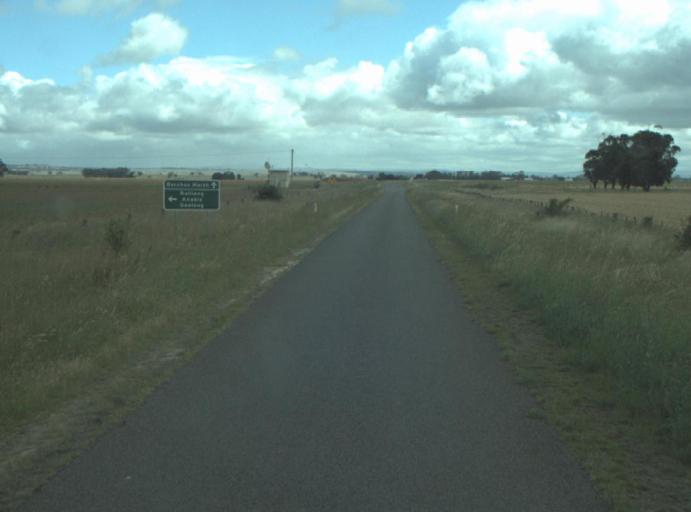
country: AU
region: Victoria
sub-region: Moorabool
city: Bacchus Marsh
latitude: -37.8361
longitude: 144.3563
